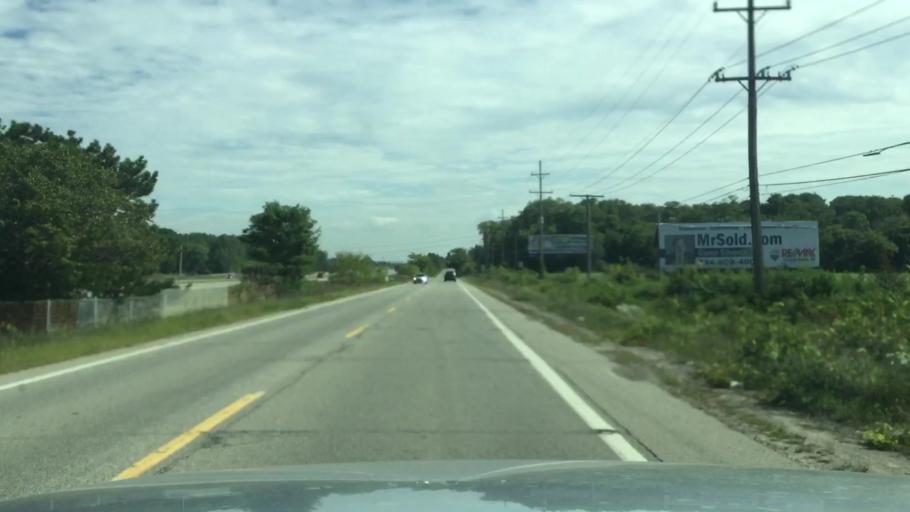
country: US
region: Michigan
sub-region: Wayne County
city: Belleville
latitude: 42.2187
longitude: -83.5078
